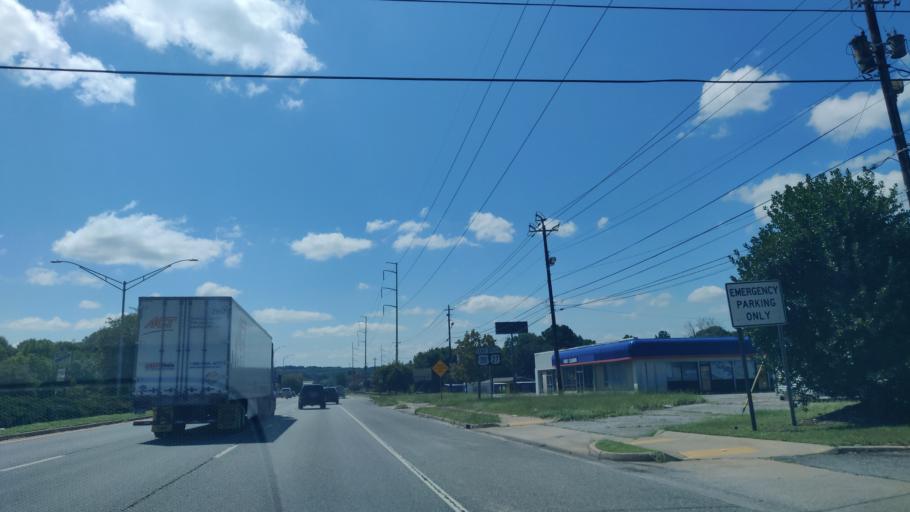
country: US
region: Georgia
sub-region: Muscogee County
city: Columbus
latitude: 32.4306
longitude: -84.9533
